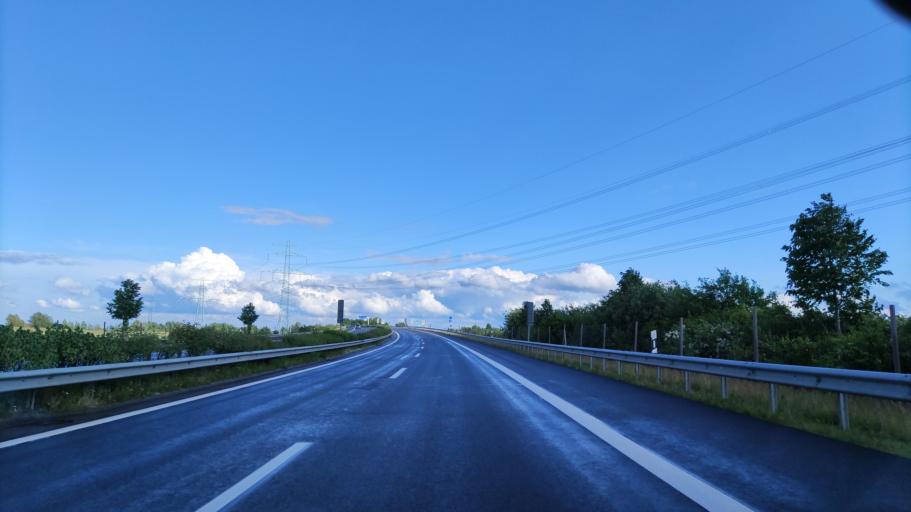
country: DE
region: Lower Saxony
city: Neuenkirchen
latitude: 53.5185
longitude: 9.5871
